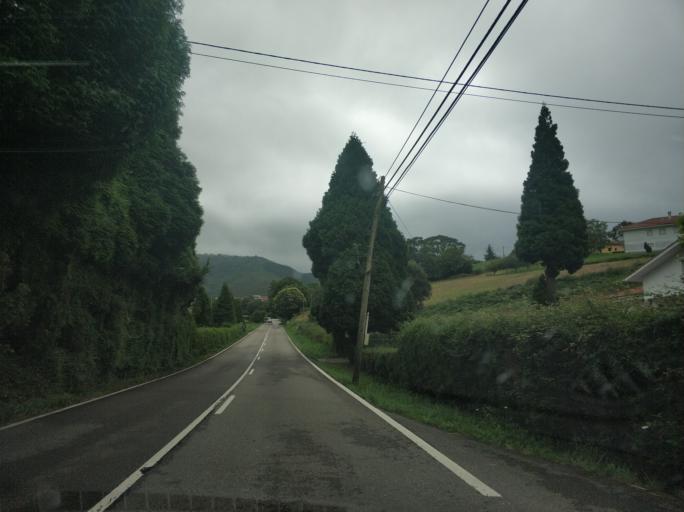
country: ES
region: Asturias
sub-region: Province of Asturias
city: Cudillero
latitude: 43.5508
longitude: -6.2255
